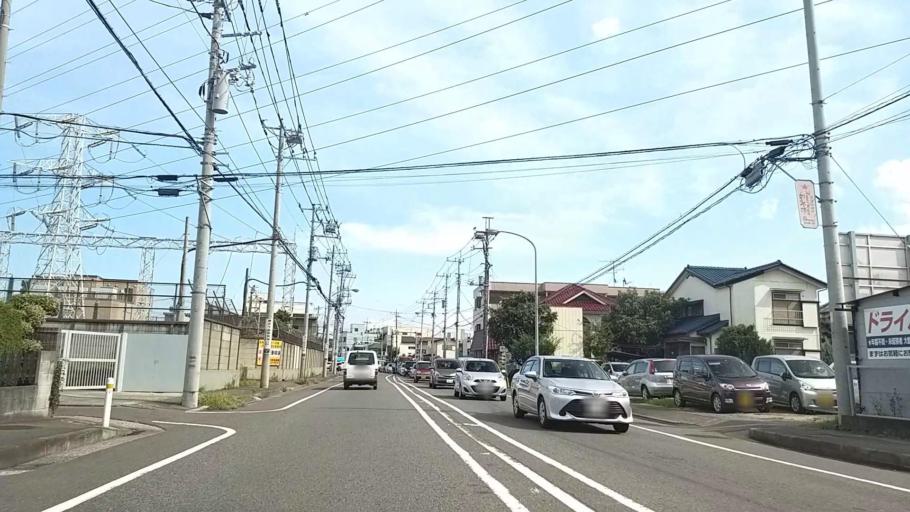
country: JP
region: Kanagawa
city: Yokohama
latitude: 35.5161
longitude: 139.5792
